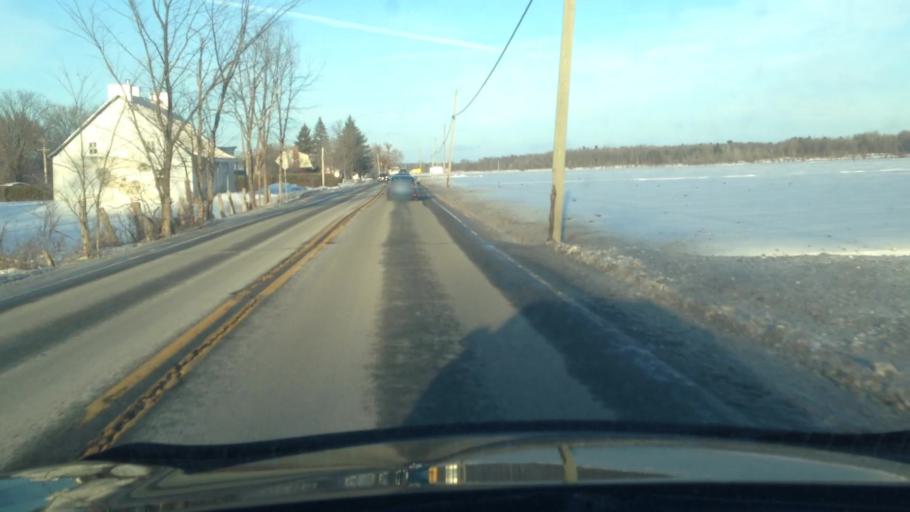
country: CA
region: Quebec
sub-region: Lanaudiere
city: Saint-Lin-Laurentides
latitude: 45.9026
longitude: -73.7495
